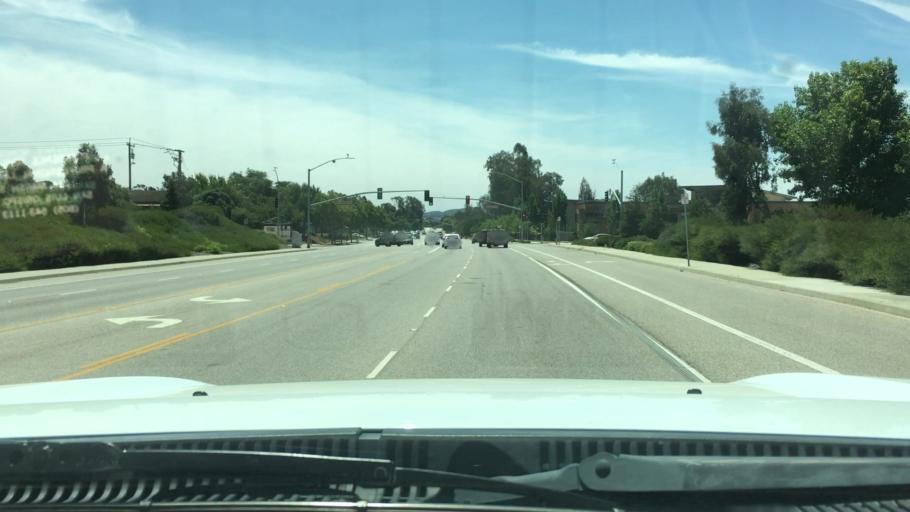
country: US
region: California
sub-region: San Luis Obispo County
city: San Luis Obispo
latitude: 35.2521
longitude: -120.6452
